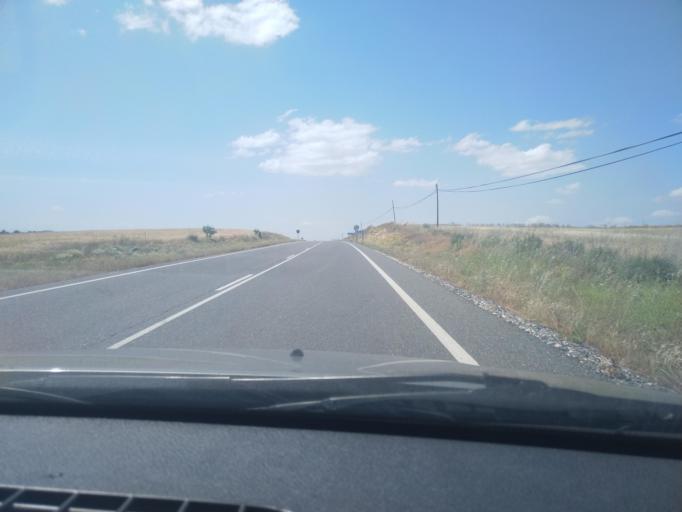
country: ES
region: Castille-La Mancha
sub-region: Province of Toledo
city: Casasbuenas
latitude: 39.7645
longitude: -4.1370
